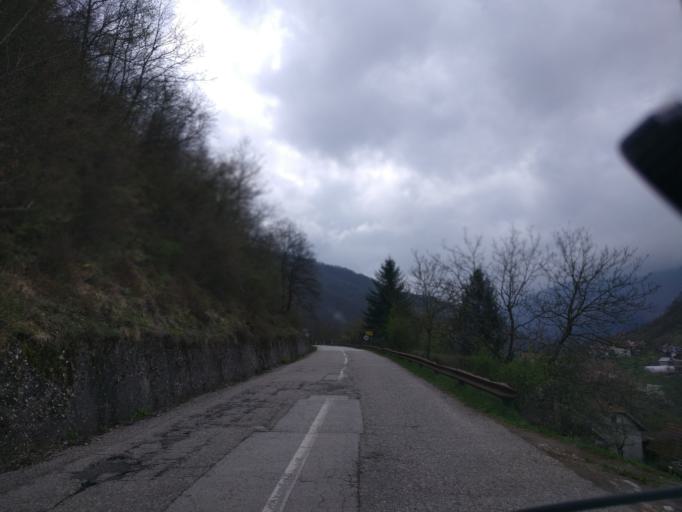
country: BA
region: Republika Srpska
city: Foca
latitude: 43.4810
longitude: 18.7480
